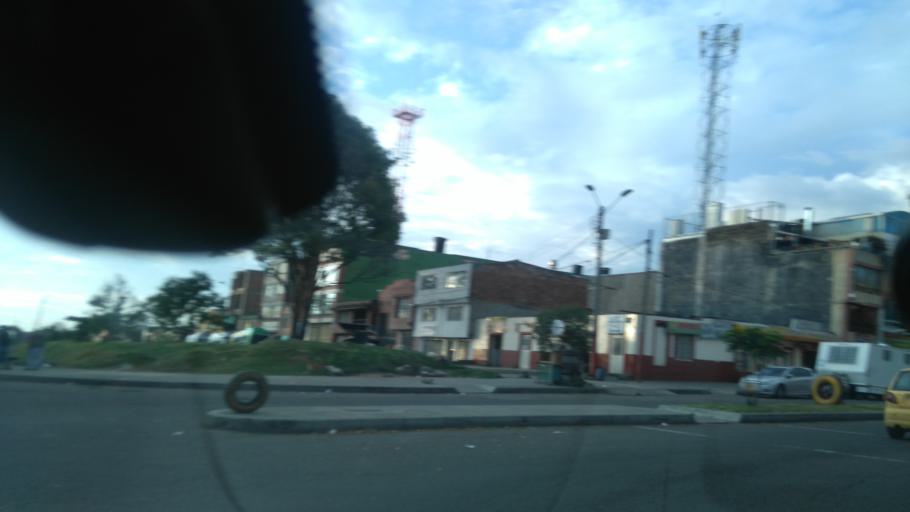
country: CO
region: Bogota D.C.
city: Bogota
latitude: 4.6427
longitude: -74.1302
